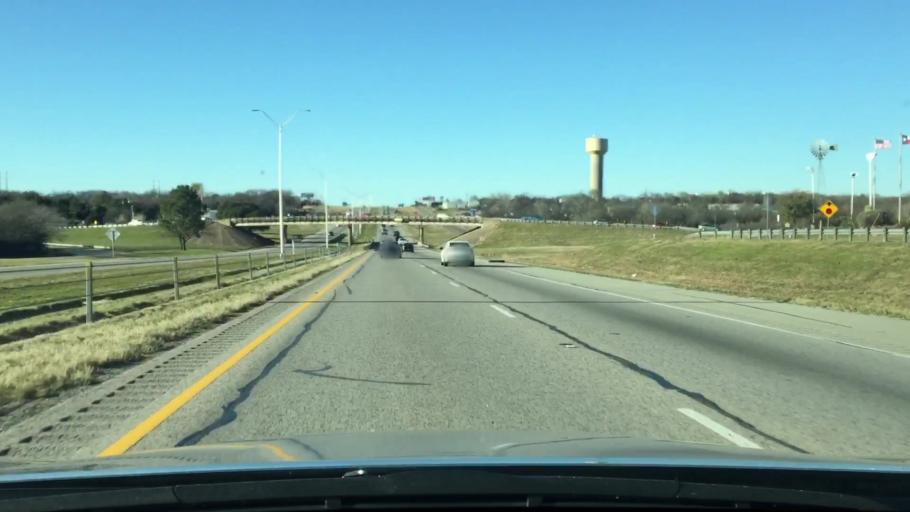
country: US
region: Texas
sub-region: Johnson County
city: Alvarado
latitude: 32.4630
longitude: -97.2651
